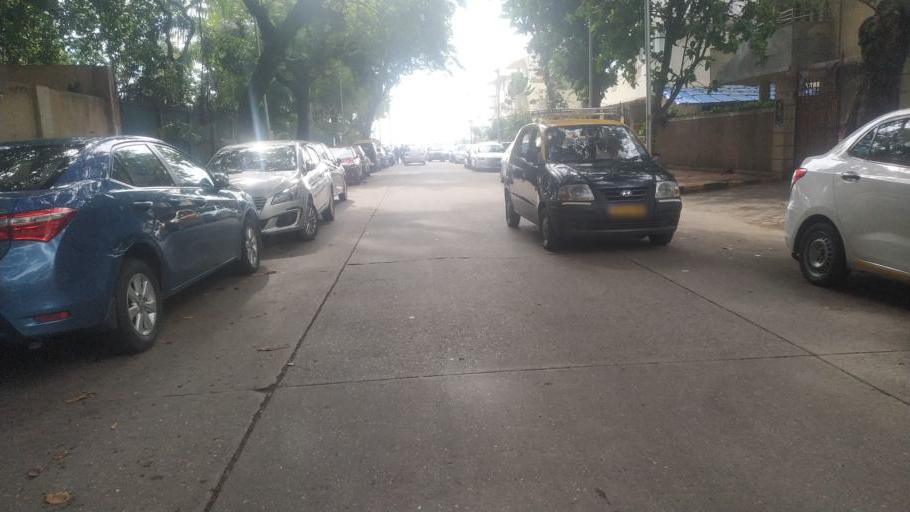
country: IN
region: Maharashtra
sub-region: Mumbai Suburban
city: Mumbai
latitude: 19.0294
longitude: 72.8375
